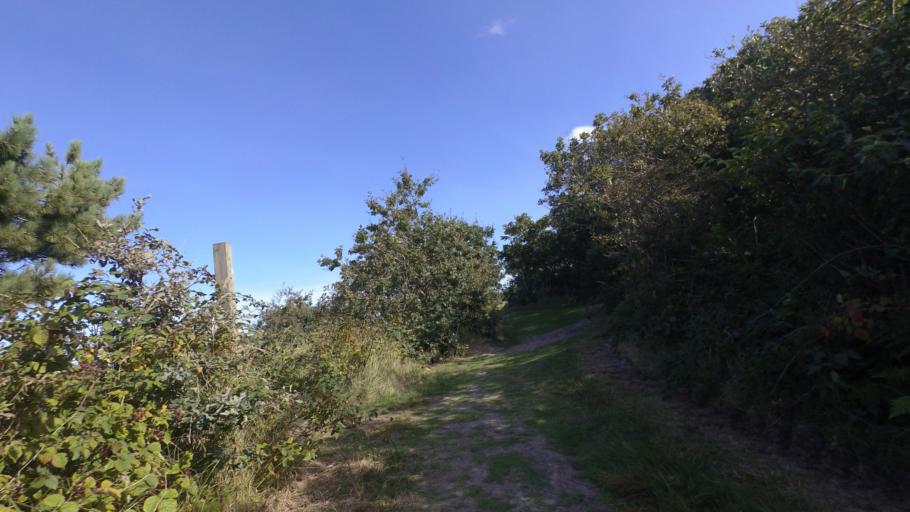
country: NL
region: Friesland
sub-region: Gemeente Ameland
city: Hollum
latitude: 53.4500
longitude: 5.7000
